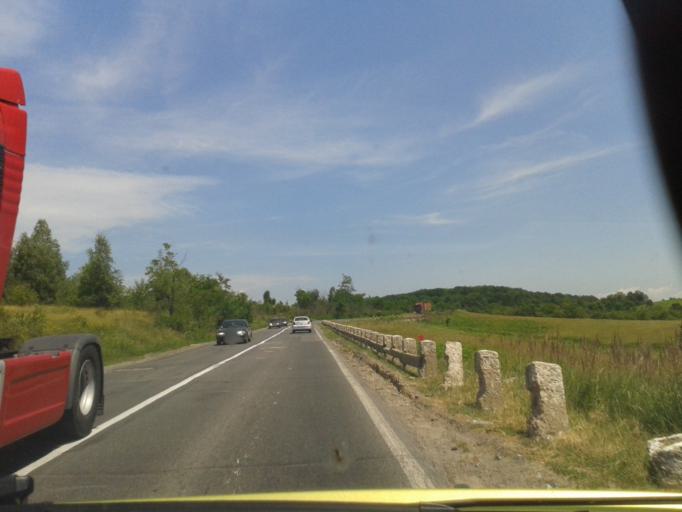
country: RO
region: Timis
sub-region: Comuna Curtea
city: Curtea
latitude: 45.8505
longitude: 22.3249
